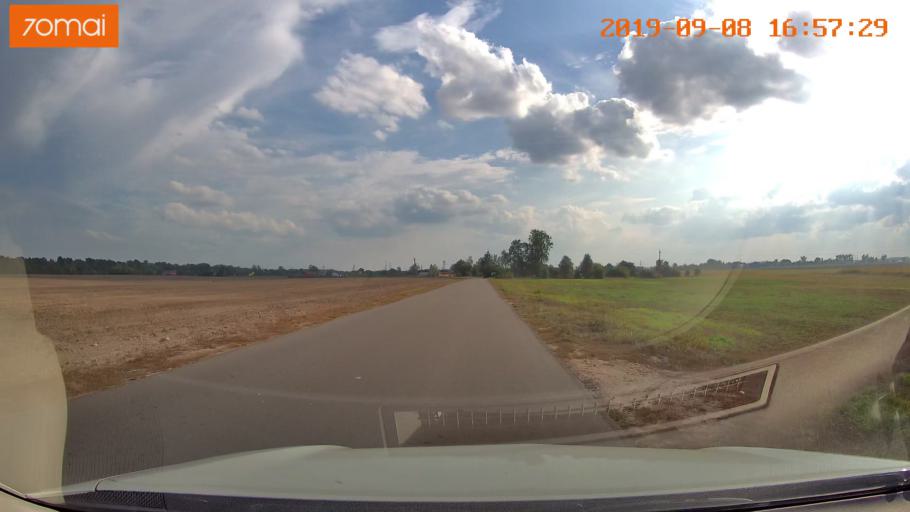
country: BY
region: Grodnenskaya
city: Hrodna
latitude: 53.7322
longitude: 23.9278
